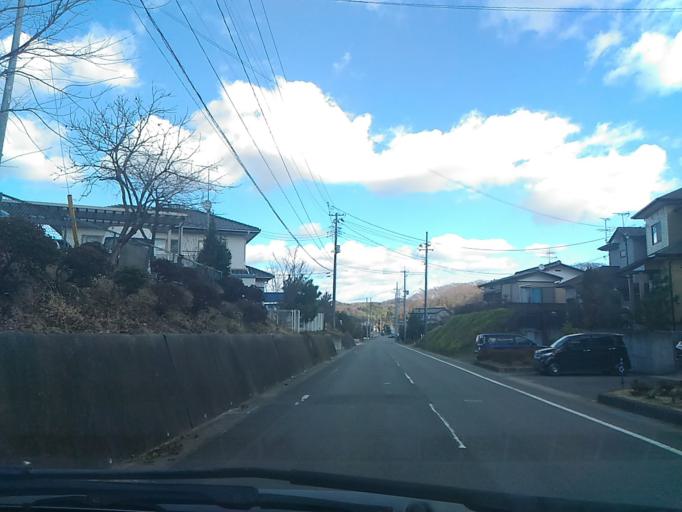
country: JP
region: Fukushima
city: Iwaki
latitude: 37.0123
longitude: 140.8355
